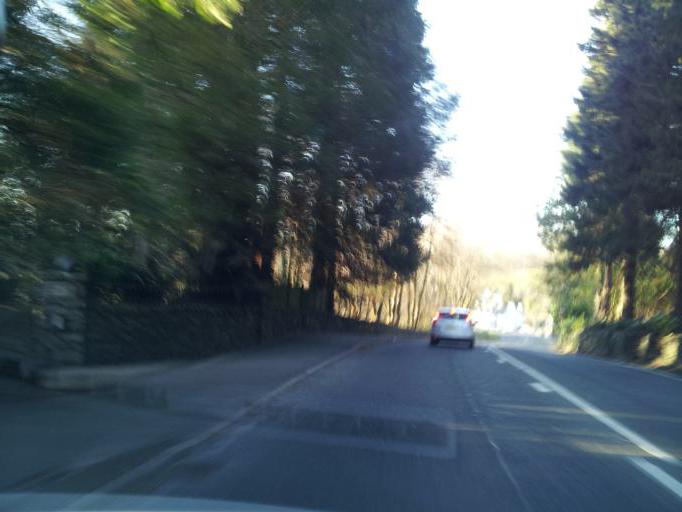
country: GB
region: England
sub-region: Cumbria
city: Windermere
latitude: 54.3916
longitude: -2.9184
